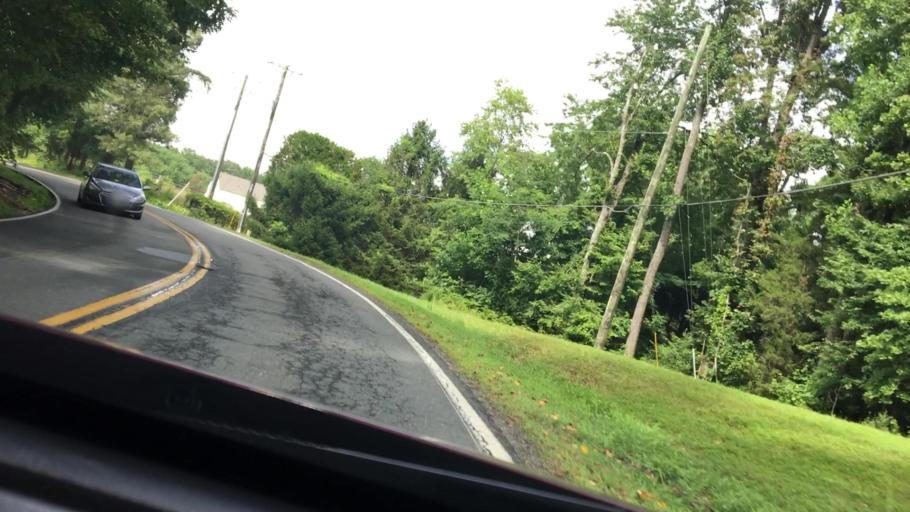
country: US
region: Virginia
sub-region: Prince William County
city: Buckhall
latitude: 38.7396
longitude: -77.4341
